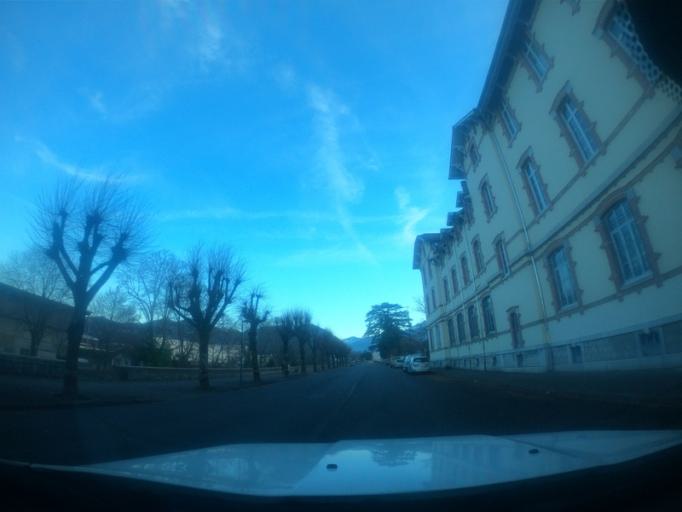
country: FR
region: Midi-Pyrenees
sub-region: Departement des Hautes-Pyrenees
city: Bagneres-de-Bigorre
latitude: 43.0632
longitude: 0.1537
